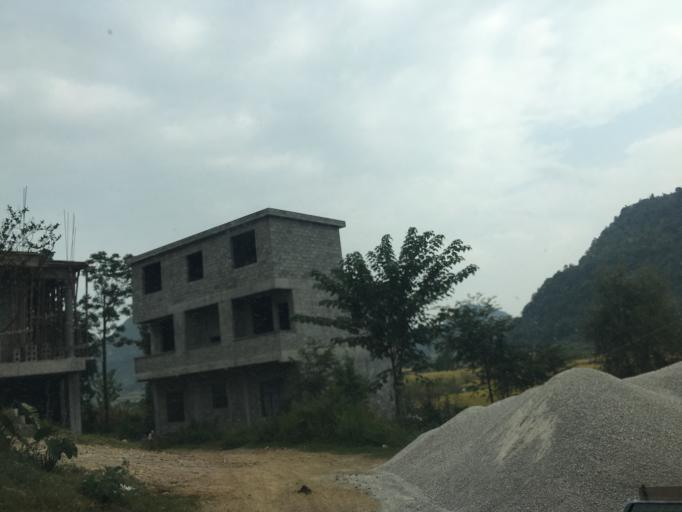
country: CN
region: Guangxi Zhuangzu Zizhiqu
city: Xinzhou
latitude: 25.4974
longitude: 105.6493
